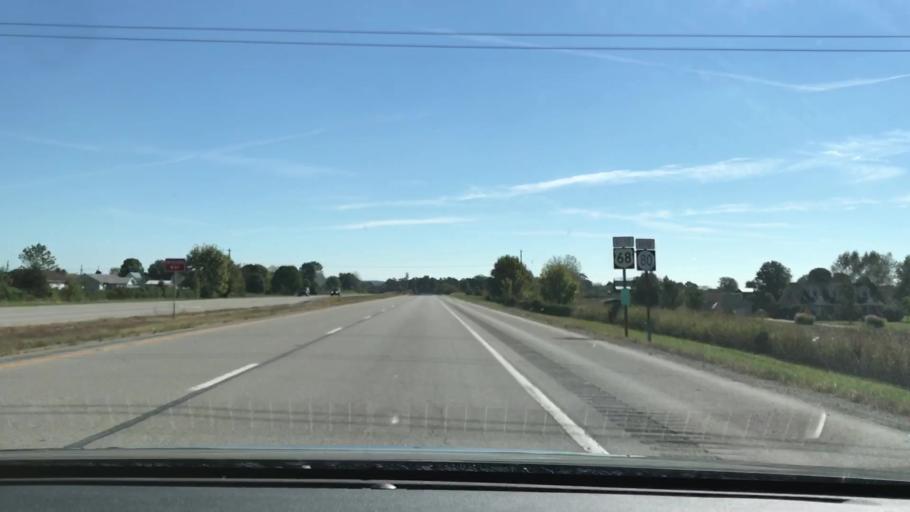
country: US
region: Kentucky
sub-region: Todd County
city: Elkton
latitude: 36.8226
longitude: -87.1991
